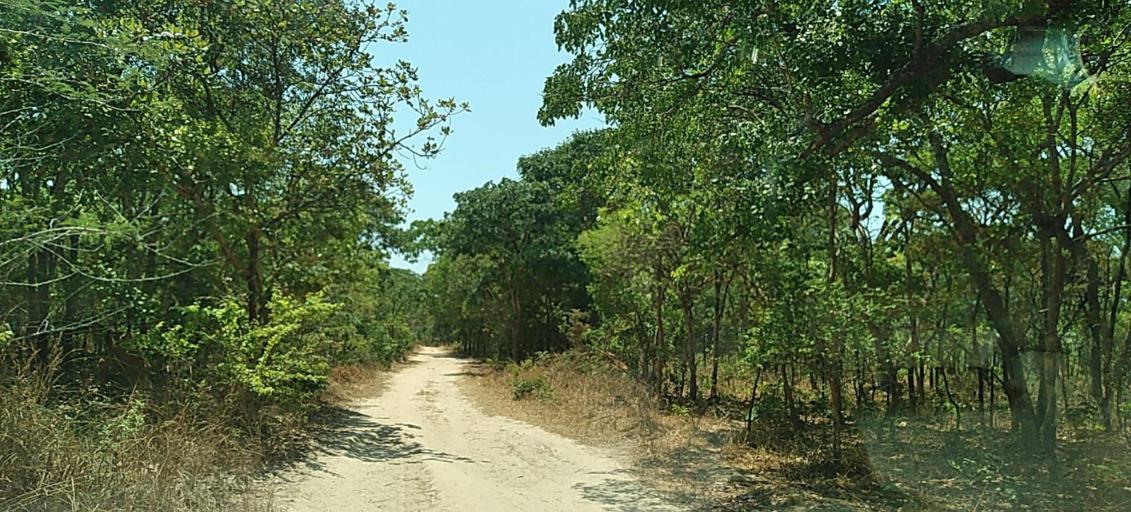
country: ZM
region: Central
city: Kapiri Mposhi
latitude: -13.6692
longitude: 28.4946
